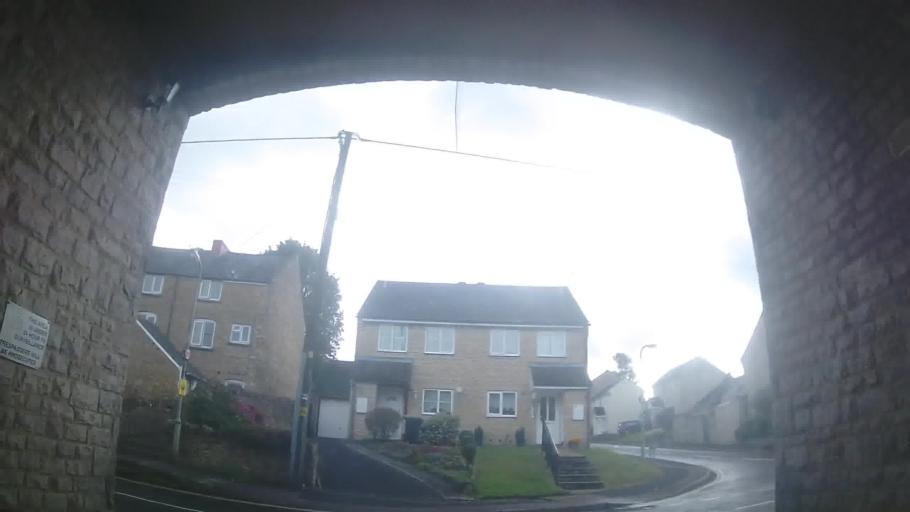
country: GB
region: England
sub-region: Oxfordshire
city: Chipping Norton
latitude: 51.9445
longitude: -1.5219
